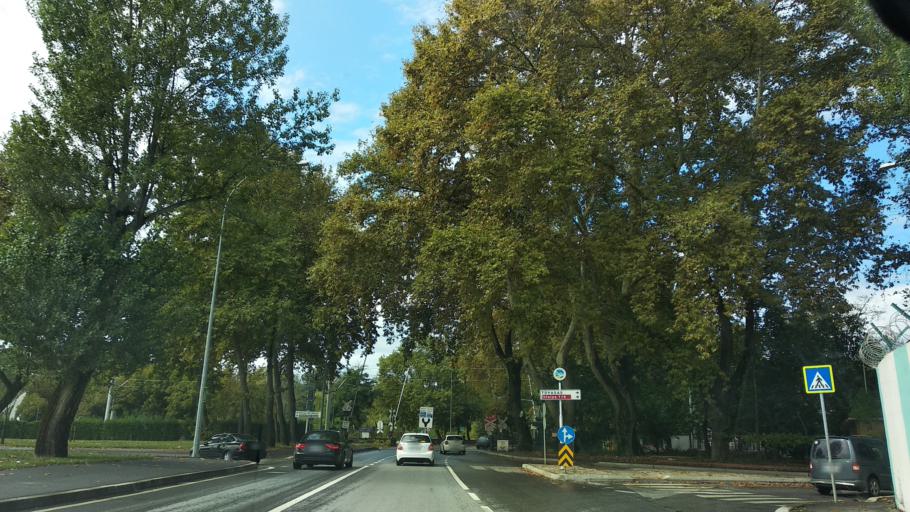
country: TR
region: Sakarya
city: Adapazari
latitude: 40.7550
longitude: 30.3776
